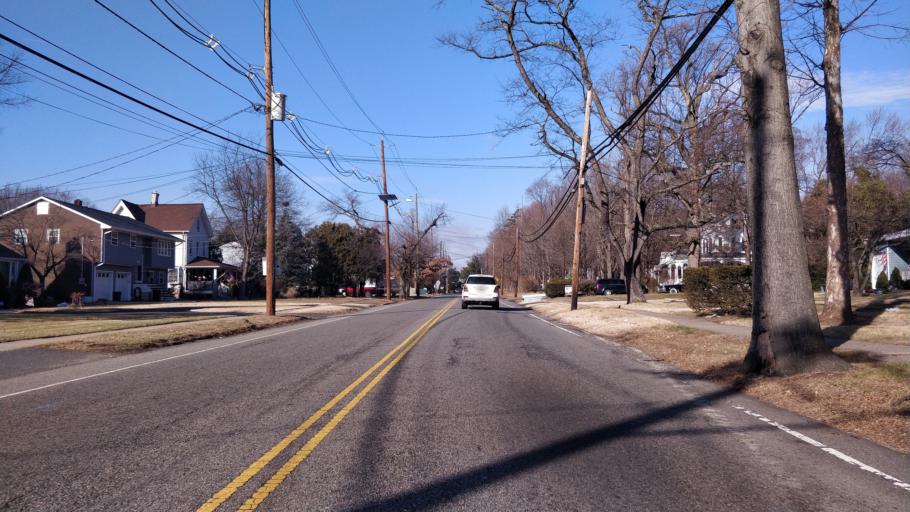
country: US
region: New Jersey
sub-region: Middlesex County
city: South Plainfield
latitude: 40.5923
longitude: -74.4334
